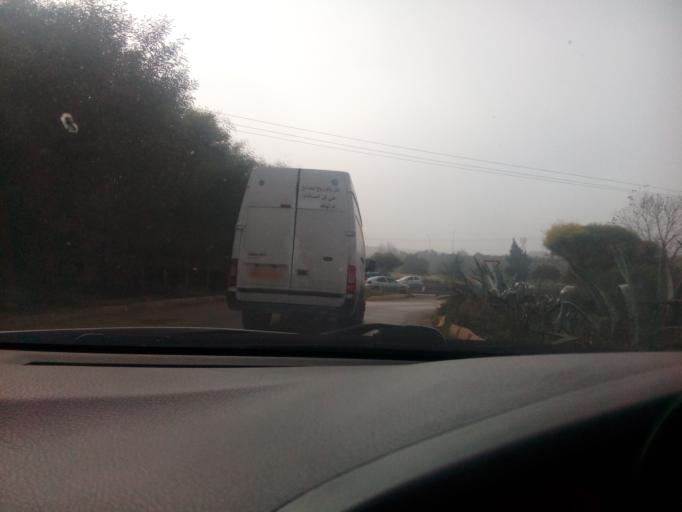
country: DZ
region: Oran
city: Es Senia
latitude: 35.6583
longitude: -0.6161
